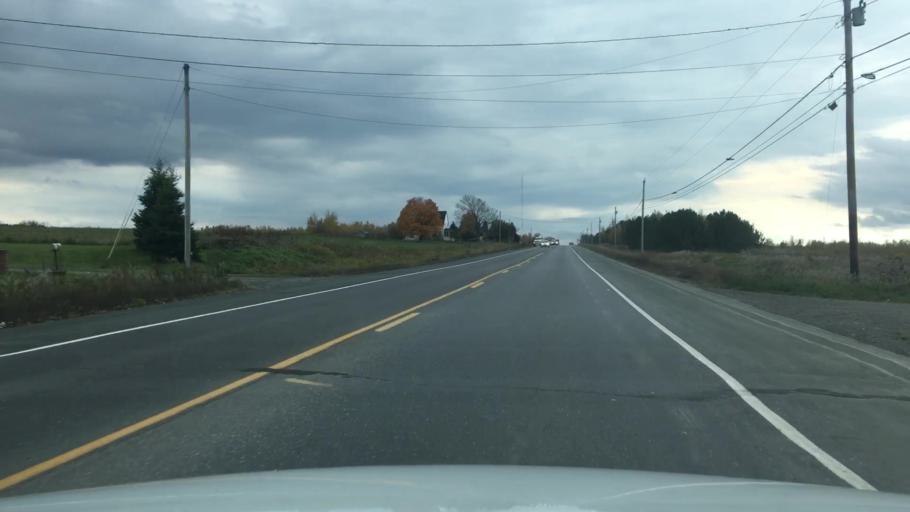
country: US
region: Maine
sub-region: Aroostook County
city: Caribou
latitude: 46.7773
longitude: -67.9893
